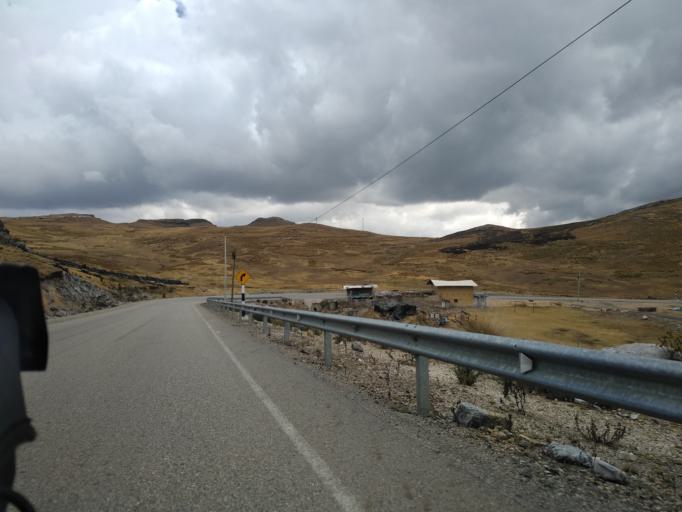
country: PE
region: La Libertad
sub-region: Provincia de Santiago de Chuco
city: Quiruvilca
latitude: -7.9891
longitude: -78.2778
